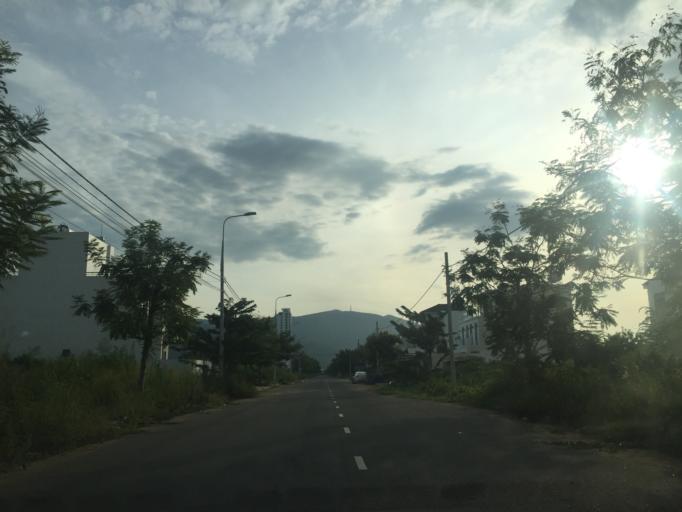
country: VN
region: Da Nang
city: Da Nang
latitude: 16.0973
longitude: 108.2267
